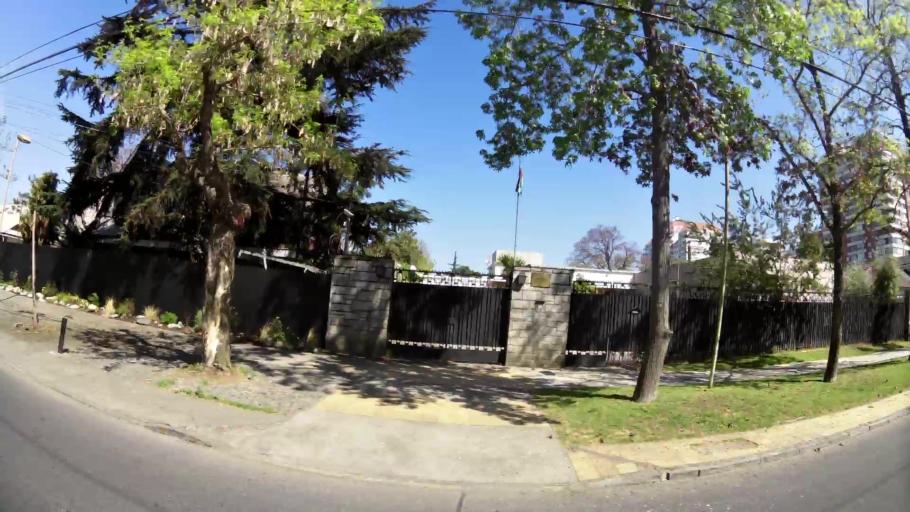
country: CL
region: Santiago Metropolitan
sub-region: Provincia de Santiago
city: Villa Presidente Frei, Nunoa, Santiago, Chile
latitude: -33.4136
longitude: -70.5750
